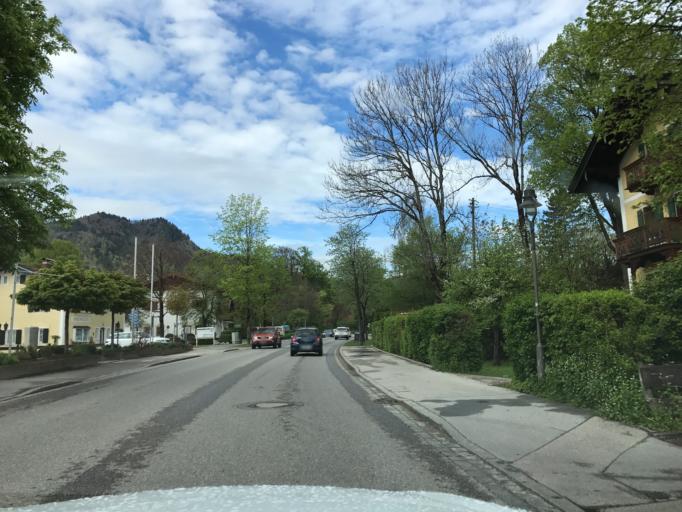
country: DE
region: Bavaria
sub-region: Upper Bavaria
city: Rottach-Egern
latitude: 47.6889
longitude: 11.7688
